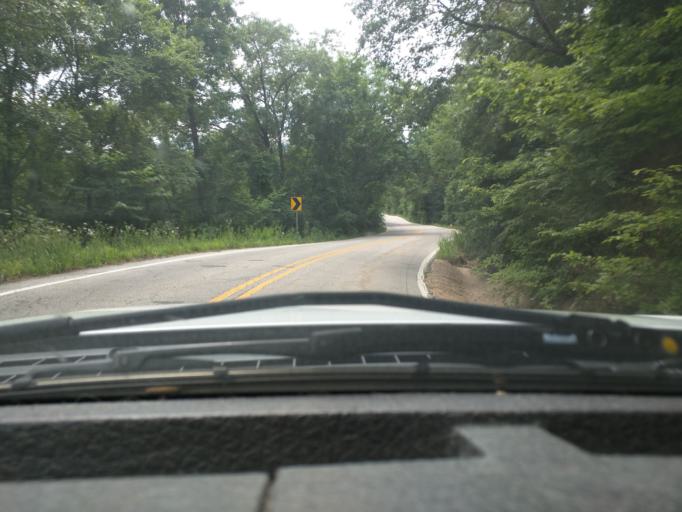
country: US
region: Arkansas
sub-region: Franklin County
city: Ozark
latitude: 35.6934
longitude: -93.8069
